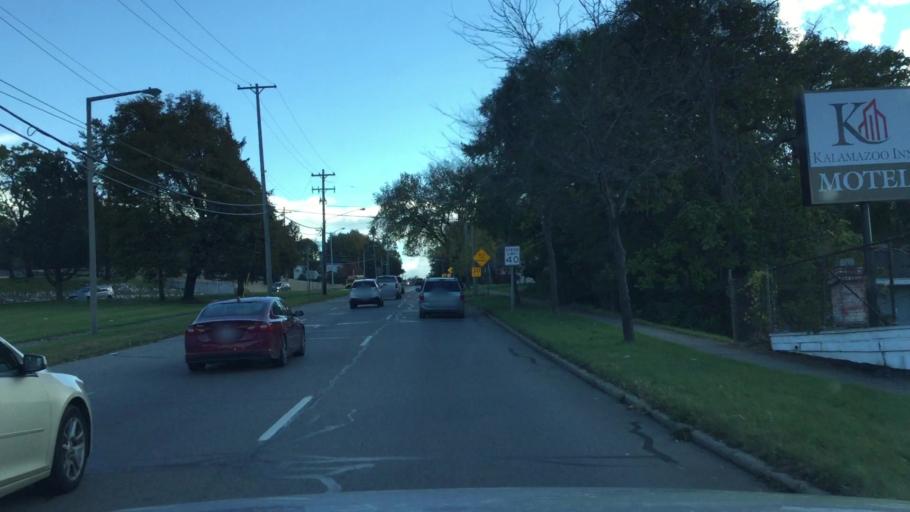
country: US
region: Michigan
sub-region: Kalamazoo County
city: Kalamazoo
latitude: 42.2724
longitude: -85.5897
